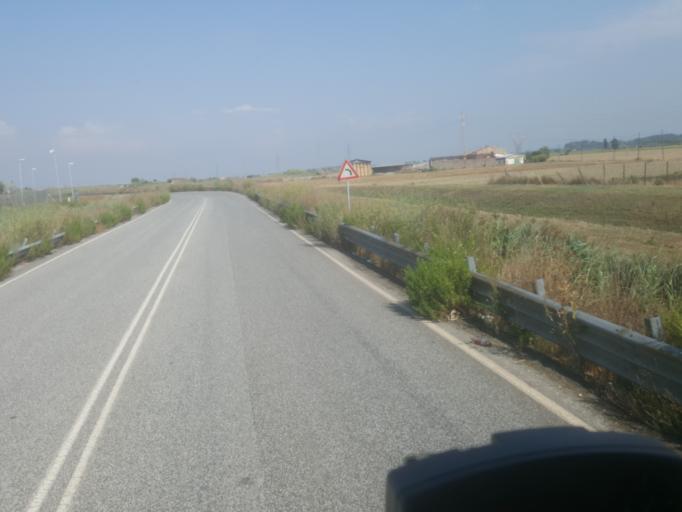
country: IT
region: Tuscany
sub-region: Provincia di Livorno
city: Guasticce
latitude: 43.6042
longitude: 10.4056
